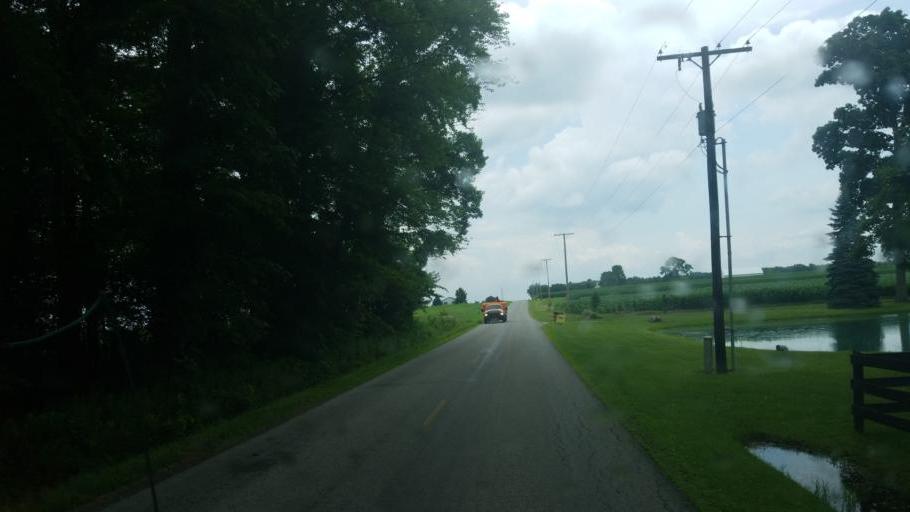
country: US
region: Ohio
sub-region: Wayne County
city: West Salem
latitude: 40.8579
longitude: -82.0949
